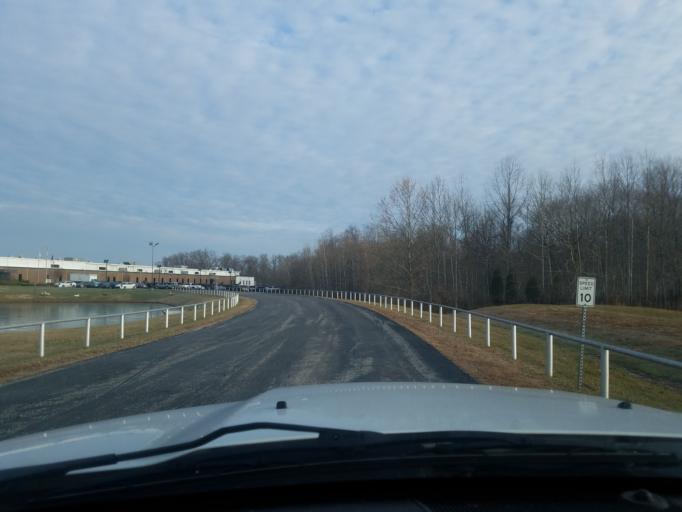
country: US
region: Indiana
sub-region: Perry County
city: Tell City
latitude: 37.9886
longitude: -86.7149
